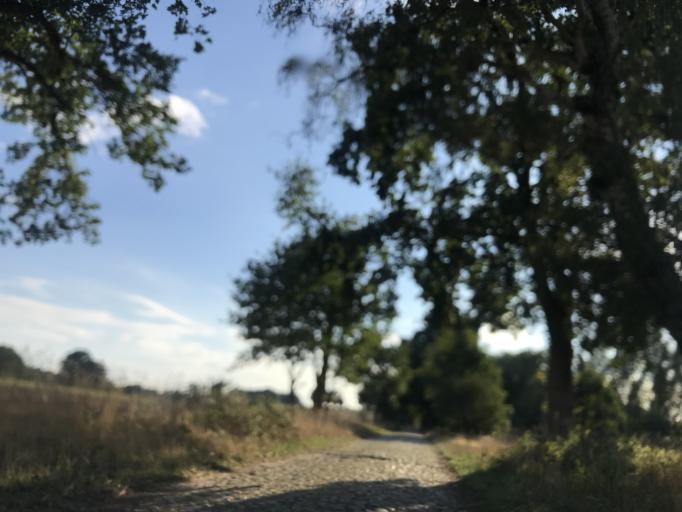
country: DE
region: Lower Saxony
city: Neetze
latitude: 53.2415
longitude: 10.6063
